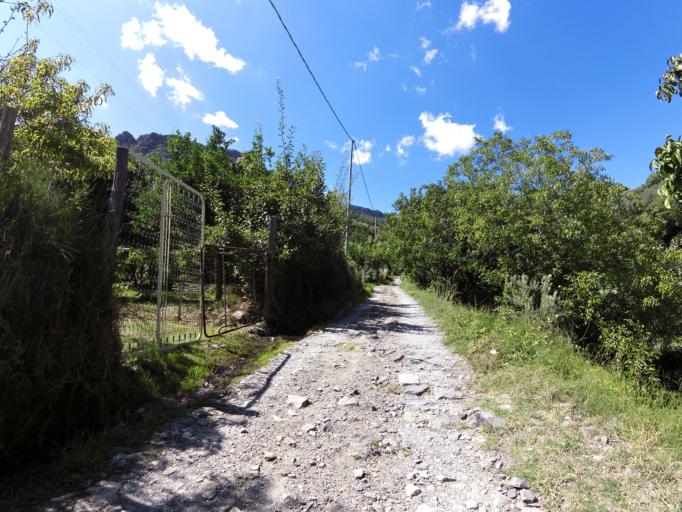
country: IT
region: Calabria
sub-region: Provincia di Reggio Calabria
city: Bivongi
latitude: 38.4817
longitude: 16.4490
